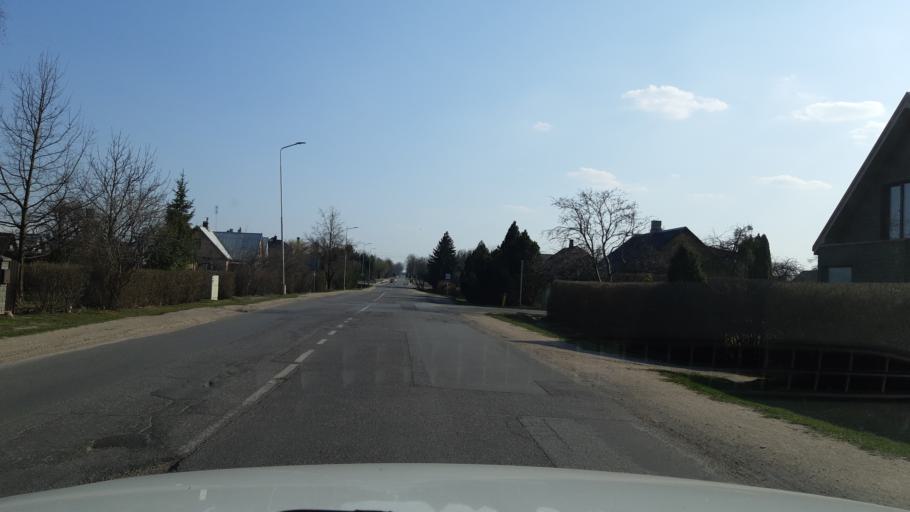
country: LT
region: Kauno apskritis
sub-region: Kaunas
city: Aleksotas
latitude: 54.8347
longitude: 23.9465
